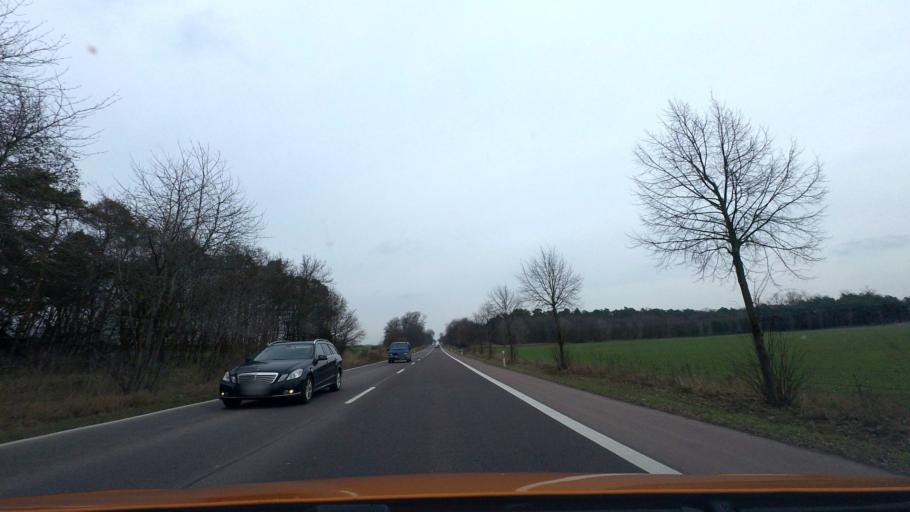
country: DE
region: Saxony-Anhalt
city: Moser
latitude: 52.1951
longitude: 11.7714
